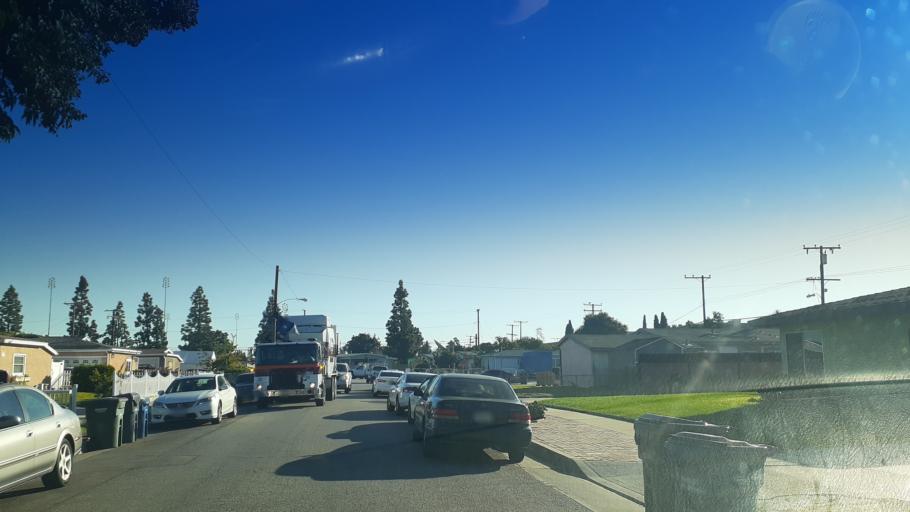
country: US
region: California
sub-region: Los Angeles County
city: Hawaiian Gardens
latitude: 33.8435
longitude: -118.0794
